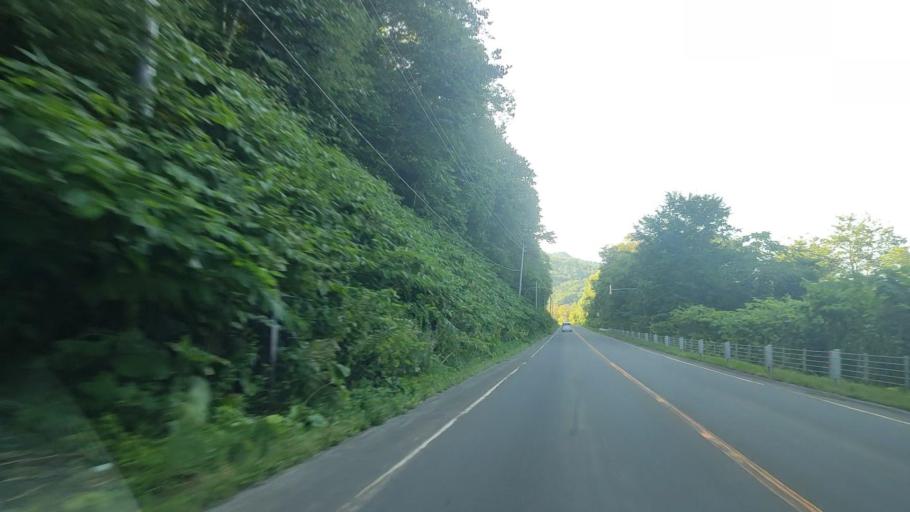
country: JP
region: Hokkaido
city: Nayoro
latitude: 44.7355
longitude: 142.1900
